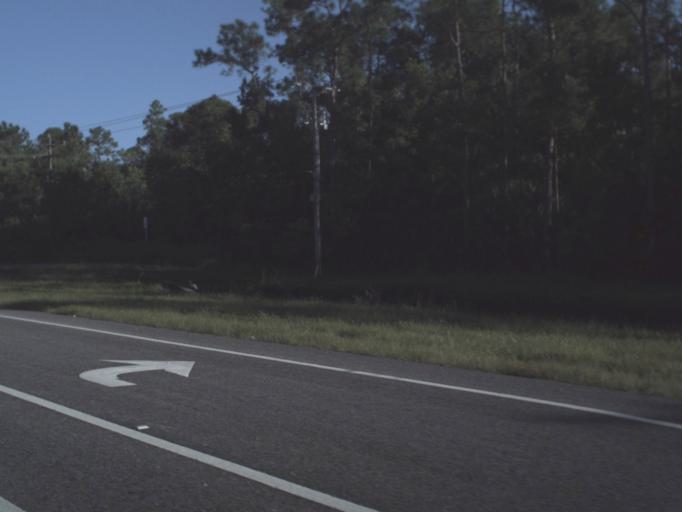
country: US
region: Florida
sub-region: Lee County
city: Suncoast Estates
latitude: 26.7489
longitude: -81.9195
